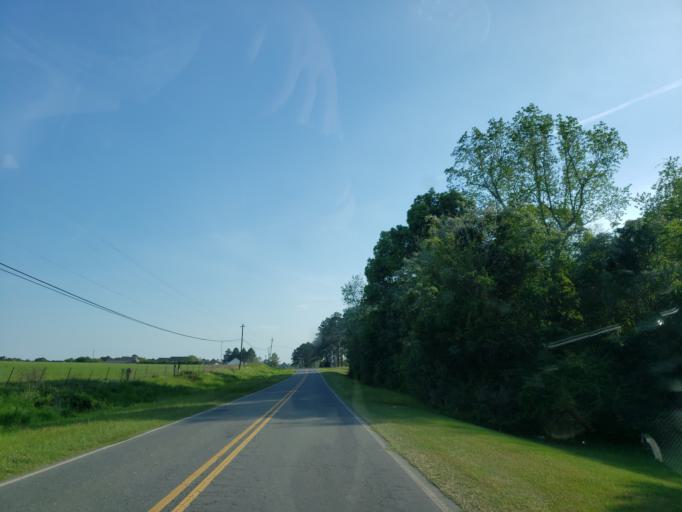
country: US
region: Georgia
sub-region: Tift County
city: Tifton
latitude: 31.4911
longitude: -83.5425
